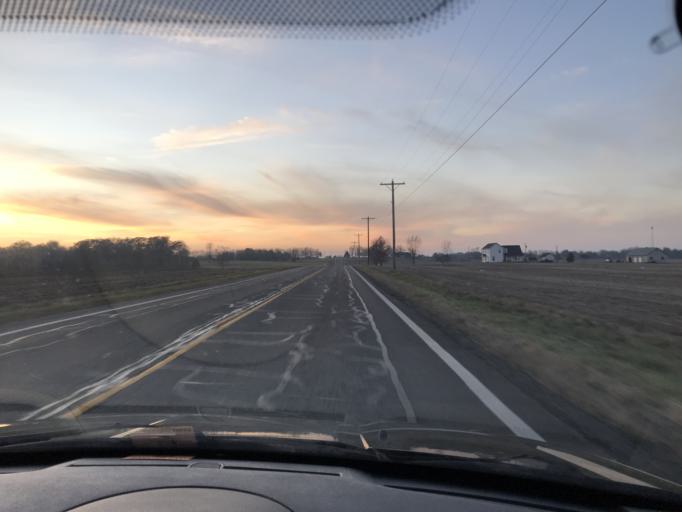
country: US
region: Ohio
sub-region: Champaign County
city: Urbana
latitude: 40.1080
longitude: -83.6939
